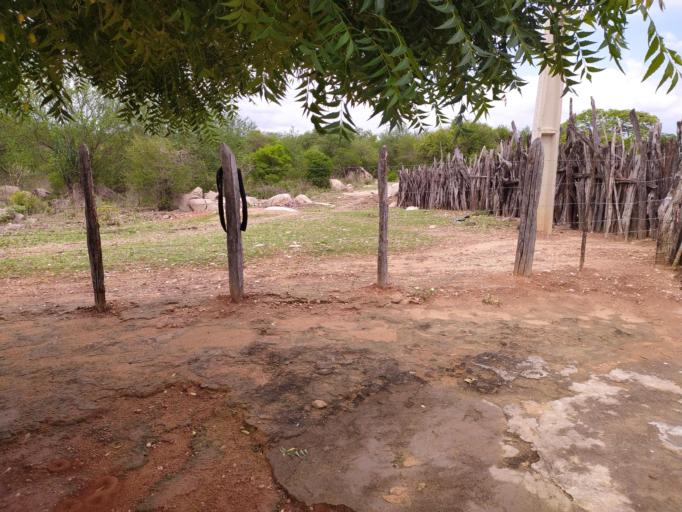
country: BR
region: Piaui
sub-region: Simplicio Mendes
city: Simplicio Mendes
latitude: -8.0950
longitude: -41.5039
